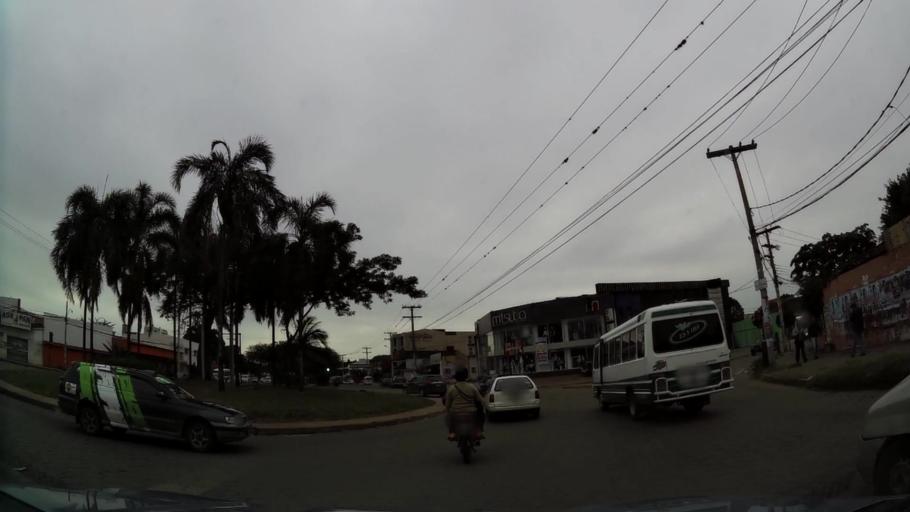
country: BO
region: Santa Cruz
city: Santa Cruz de la Sierra
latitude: -17.7783
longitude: -63.1729
